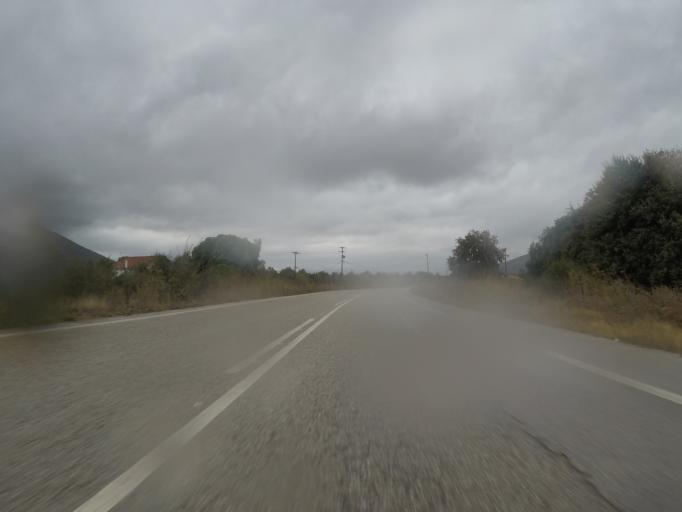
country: GR
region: Peloponnese
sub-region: Nomos Arkadias
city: Tripoli
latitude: 37.5885
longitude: 22.4267
